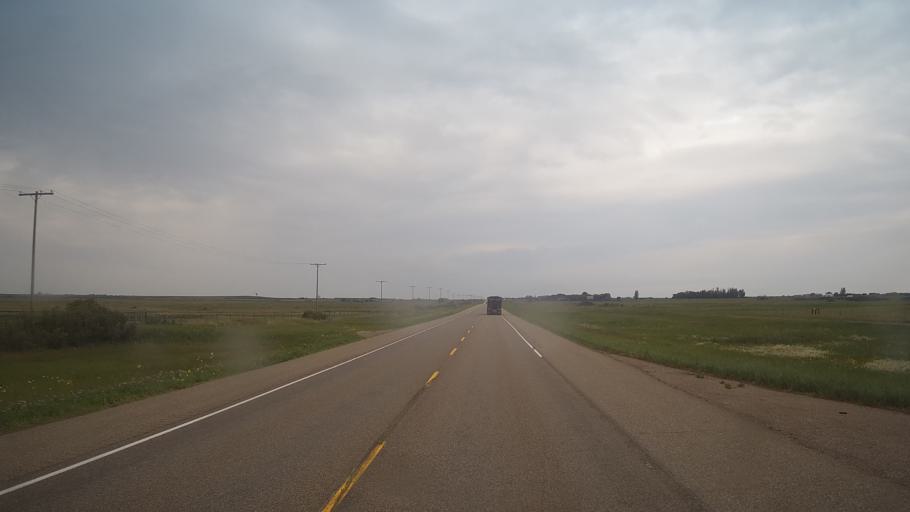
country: CA
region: Saskatchewan
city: Langham
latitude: 52.1289
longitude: -107.1501
